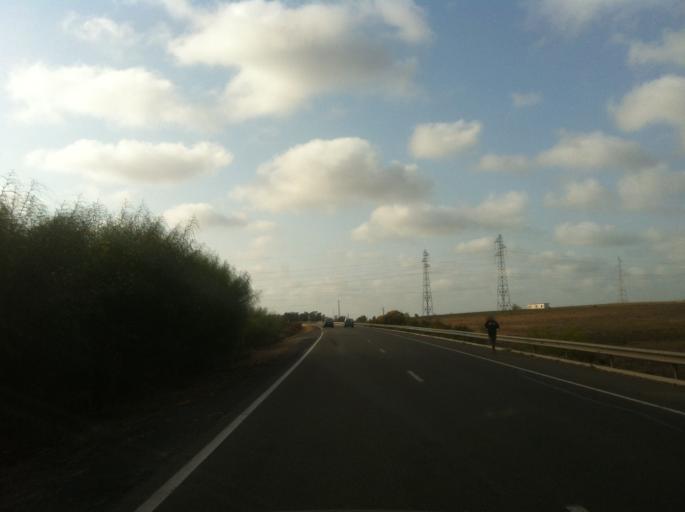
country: MA
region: Gharb-Chrarda-Beni Hssen
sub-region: Kenitra Province
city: Kenitra
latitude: 34.2229
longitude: -6.5376
